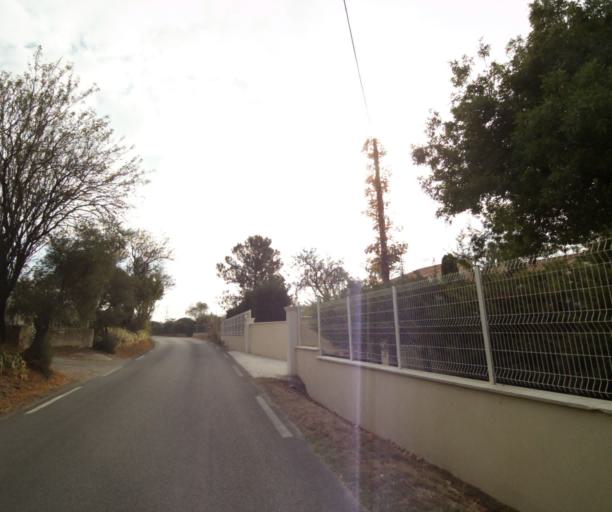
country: FR
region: Provence-Alpes-Cote d'Azur
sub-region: Departement des Bouches-du-Rhone
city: Saint-Victoret
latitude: 43.4081
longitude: 5.2723
